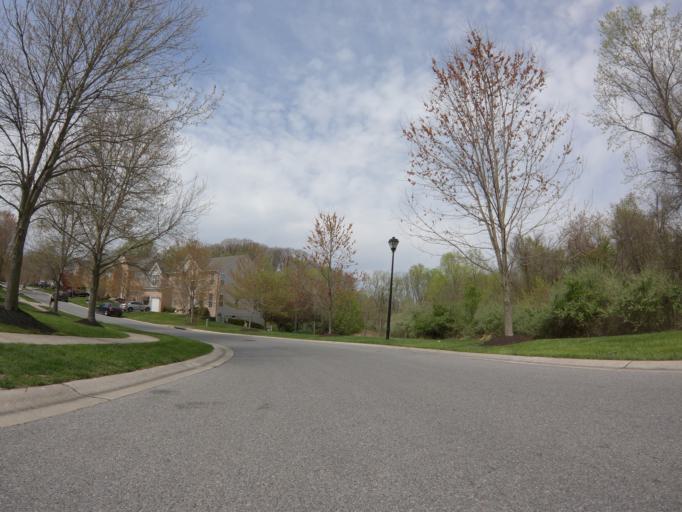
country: US
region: Maryland
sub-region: Howard County
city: Ellicott City
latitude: 39.2509
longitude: -76.7950
